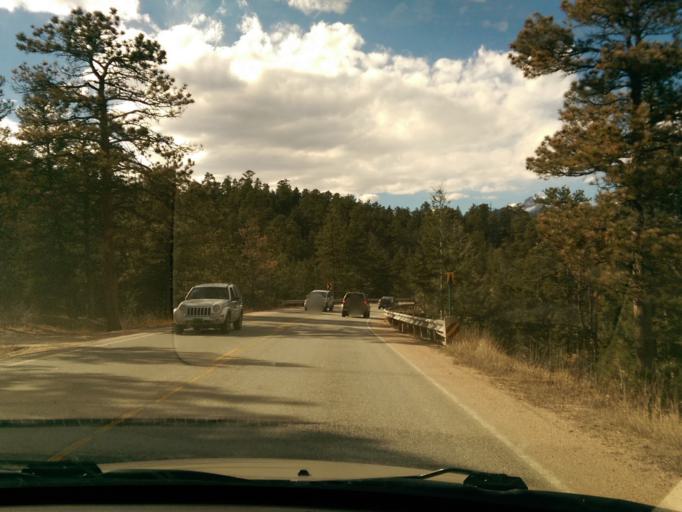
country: US
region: Colorado
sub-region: Larimer County
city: Estes Park
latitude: 40.3638
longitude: -105.4711
